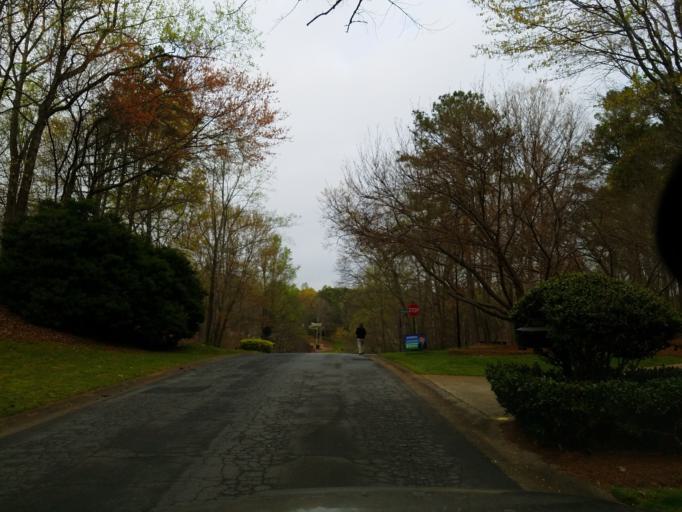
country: US
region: Georgia
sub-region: Fulton County
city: Roswell
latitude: 34.0342
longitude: -84.4228
